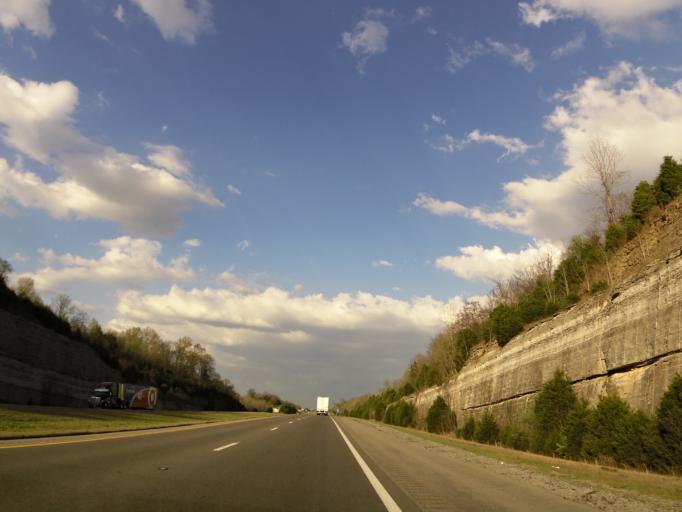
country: US
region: Tennessee
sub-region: Wilson County
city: Rural Hill
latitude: 36.1386
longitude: -86.3827
